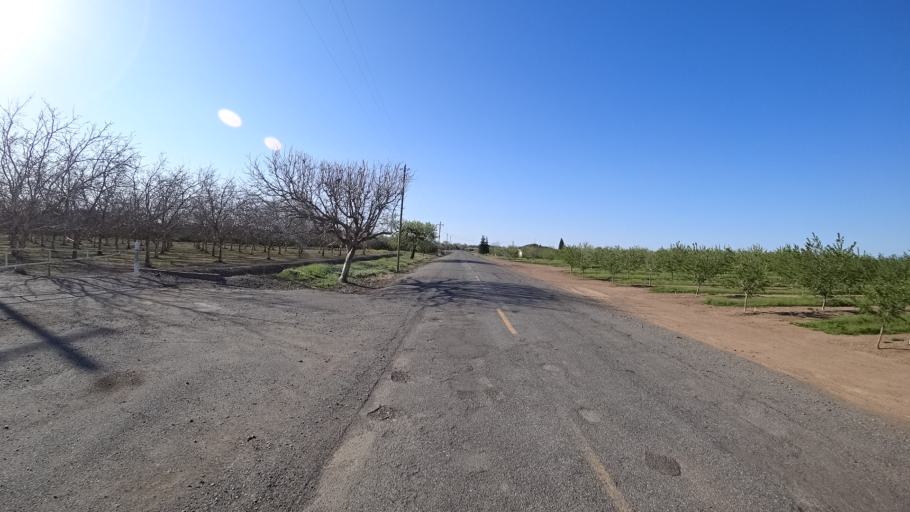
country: US
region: California
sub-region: Glenn County
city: Orland
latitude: 39.7653
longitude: -122.1321
